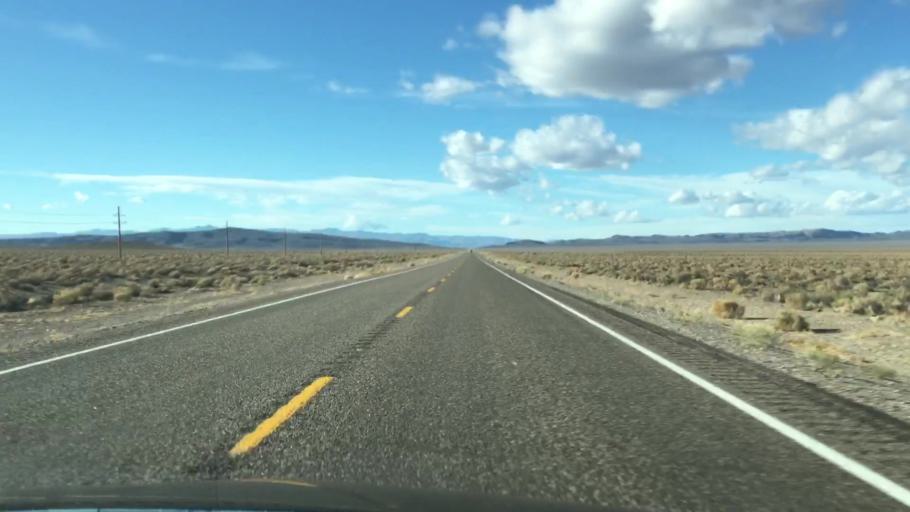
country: US
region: Nevada
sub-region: Nye County
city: Beatty
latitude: 37.1281
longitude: -116.8370
